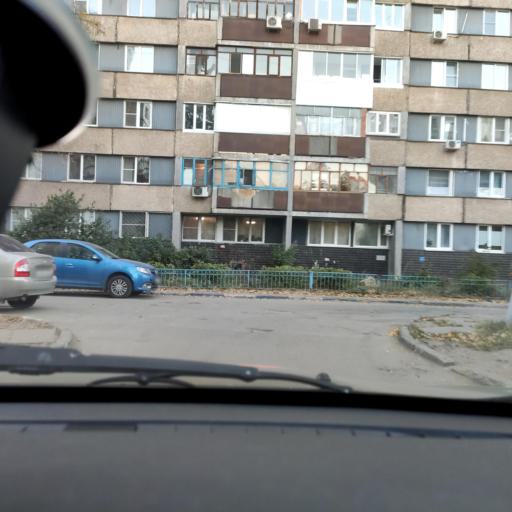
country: RU
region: Samara
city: Tol'yatti
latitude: 53.5340
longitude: 49.2848
